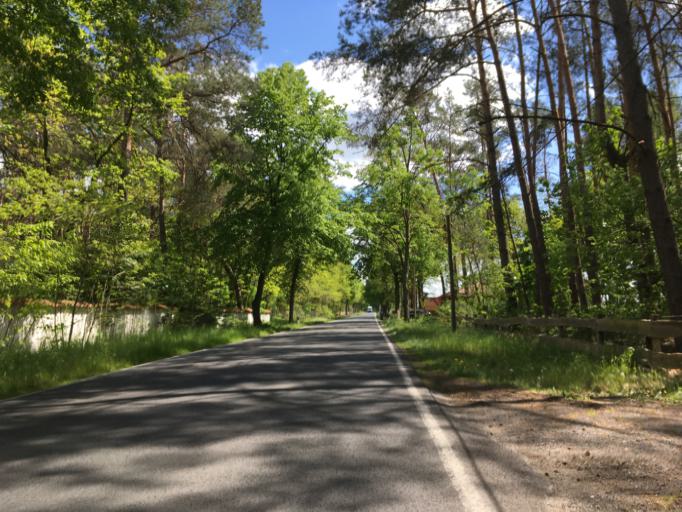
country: DE
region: Brandenburg
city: Wandlitz
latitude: 52.7855
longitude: 13.4144
